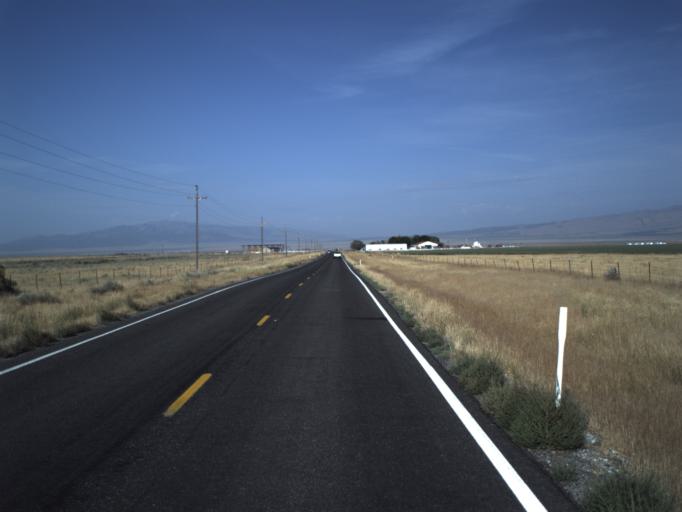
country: US
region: Idaho
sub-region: Oneida County
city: Malad City
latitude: 41.9670
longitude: -112.7950
